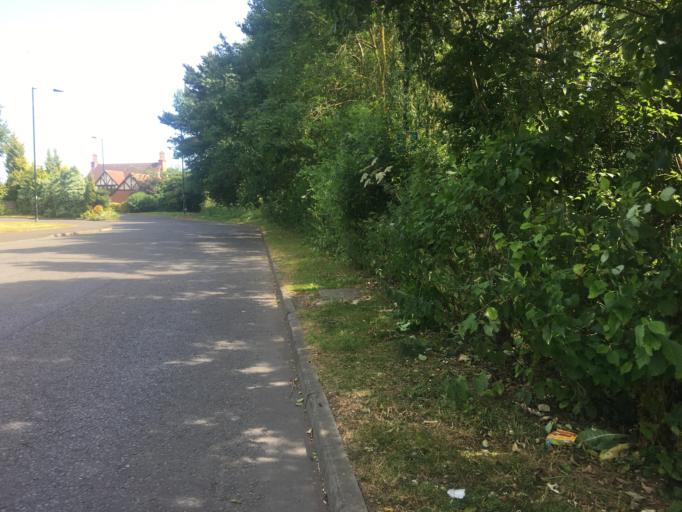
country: GB
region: England
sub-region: Sunderland
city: Washington
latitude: 54.8771
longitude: -1.5437
